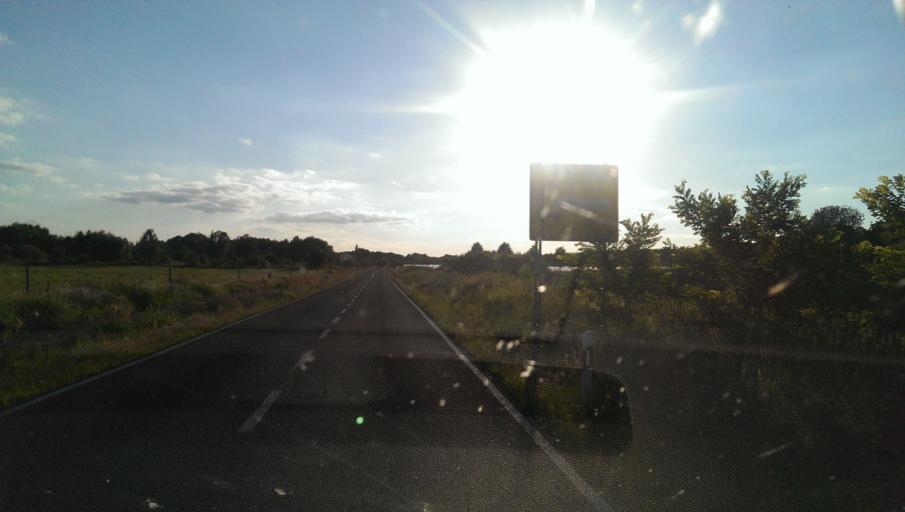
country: DE
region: Brandenburg
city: Trebbin
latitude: 52.2386
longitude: 13.1534
